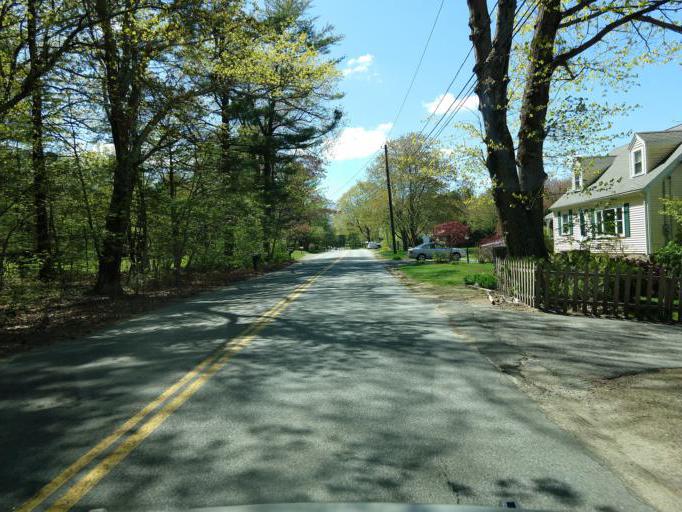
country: US
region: New Hampshire
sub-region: Rockingham County
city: Seabrook
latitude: 42.8830
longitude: -70.8920
